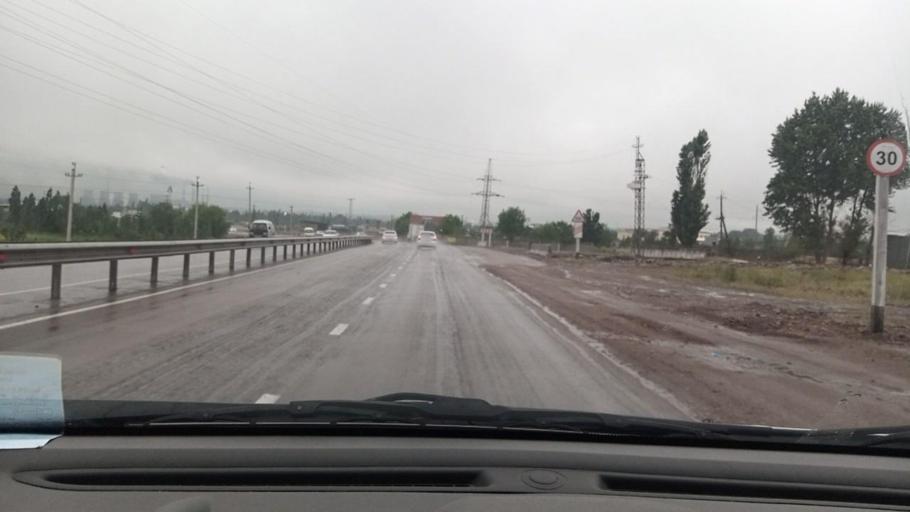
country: UZ
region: Toshkent
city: Angren
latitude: 41.0318
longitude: 70.1388
